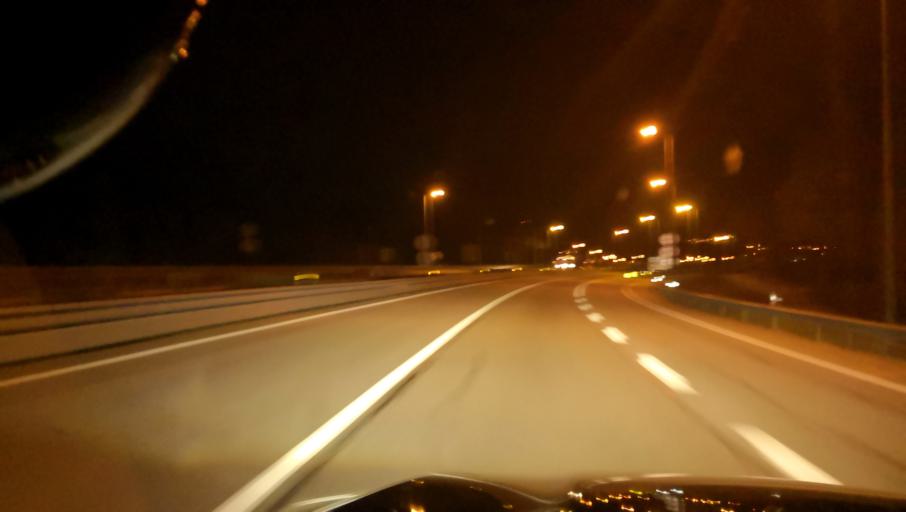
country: PT
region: Viseu
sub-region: Oliveira de Frades
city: Oliveira de Frades
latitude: 40.6824
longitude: -8.1952
